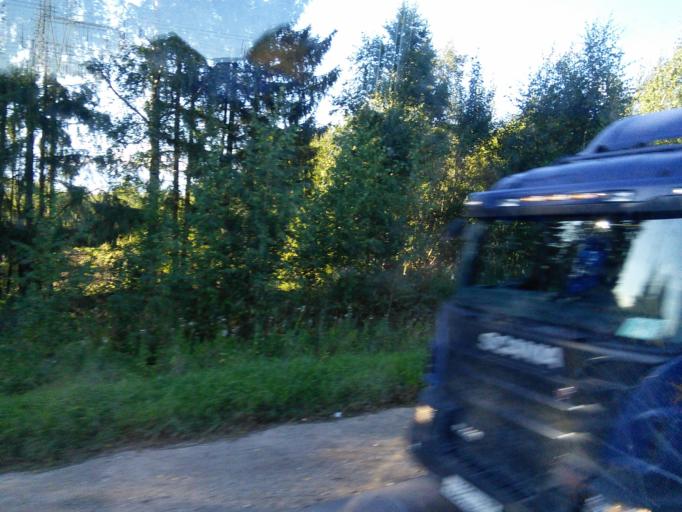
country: RU
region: Jaroslavl
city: Poshekhon'ye
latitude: 58.4943
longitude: 39.0938
